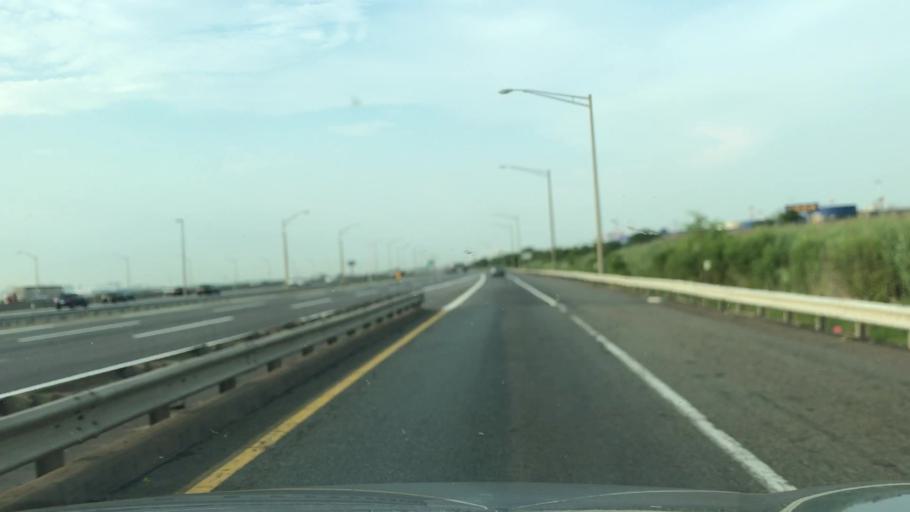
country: US
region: New Jersey
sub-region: Union County
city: Elizabeth
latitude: 40.6729
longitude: -74.1740
